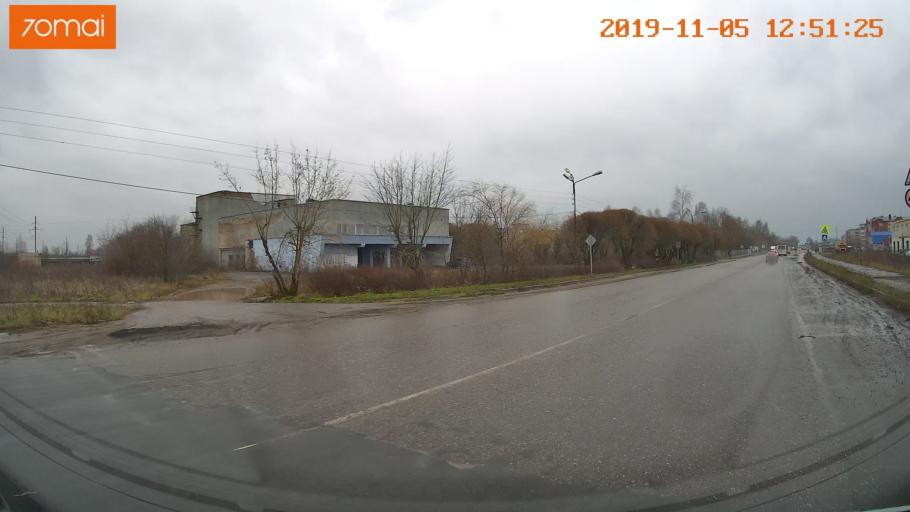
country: RU
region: Ivanovo
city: Kokhma
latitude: 56.9430
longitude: 41.1144
